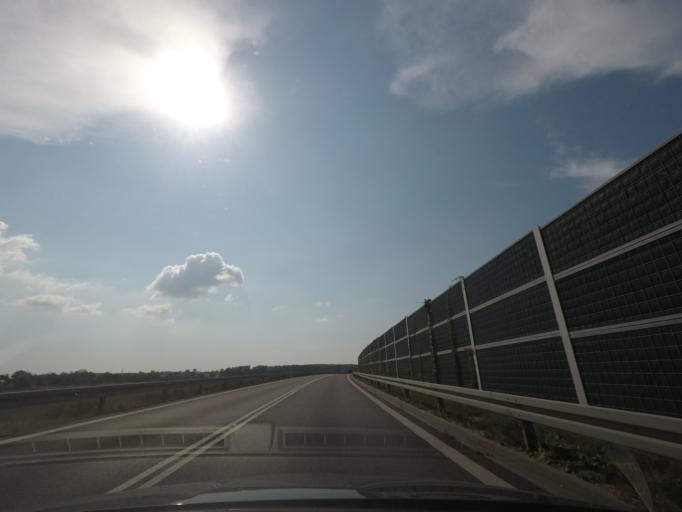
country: PL
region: Silesian Voivodeship
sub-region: Powiat pszczynski
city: Czarkow
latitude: 50.0015
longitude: 18.9198
